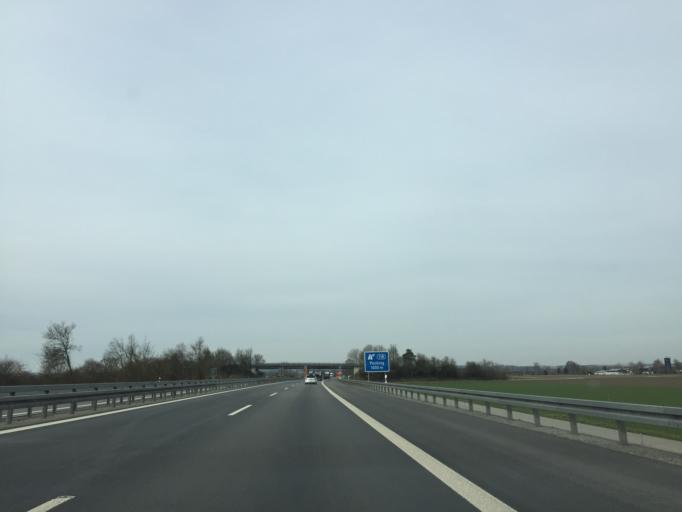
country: AT
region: Upper Austria
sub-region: Politischer Bezirk Scharding
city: Scharding
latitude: 48.4247
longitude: 13.3887
